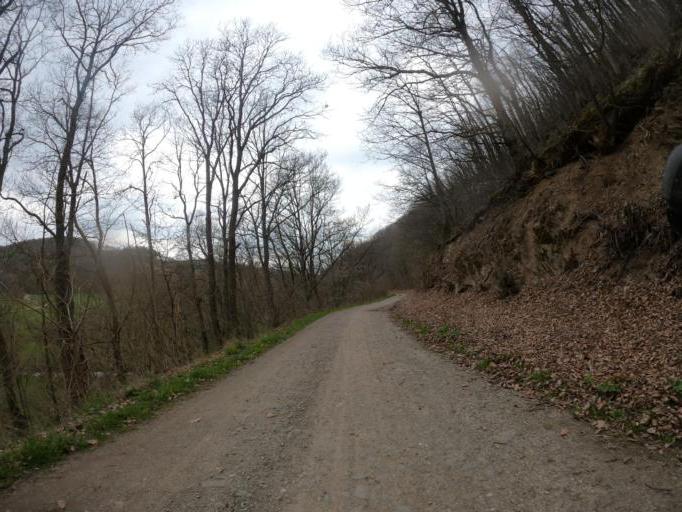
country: DE
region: North Rhine-Westphalia
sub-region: Regierungsbezirk Koln
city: Nideggen
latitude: 50.6809
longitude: 6.4257
